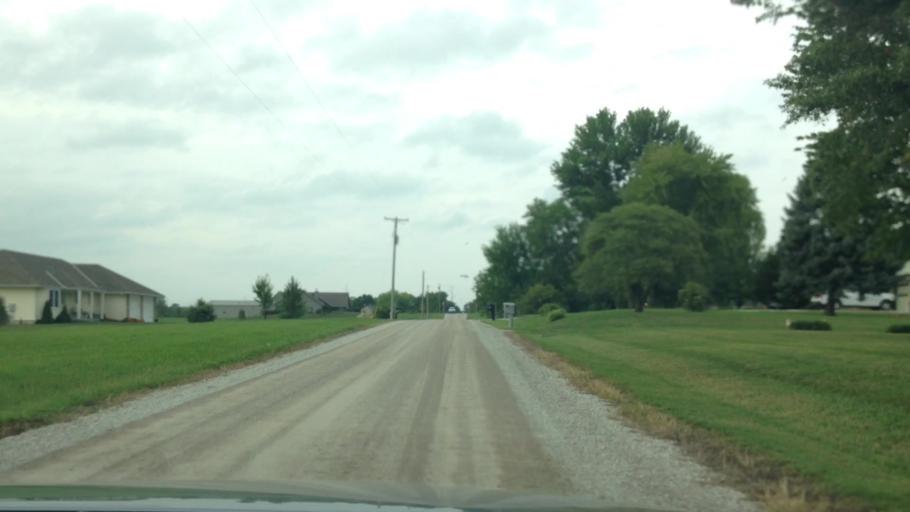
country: US
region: Missouri
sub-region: Clay County
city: Smithville
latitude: 39.3999
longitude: -94.6435
